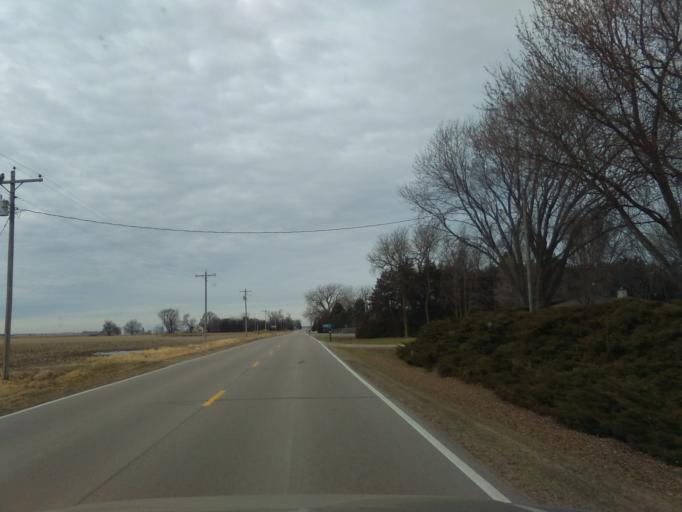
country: US
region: Nebraska
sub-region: Hall County
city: Grand Island
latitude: 40.7709
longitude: -98.4103
